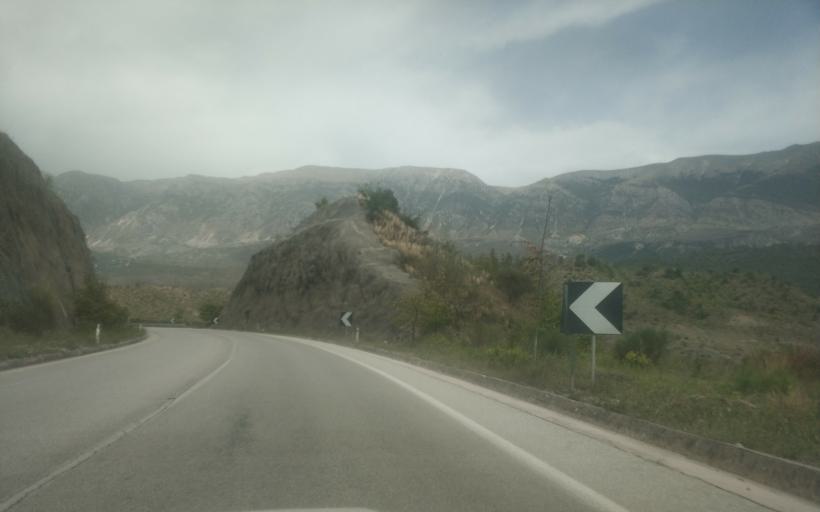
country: AL
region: Gjirokaster
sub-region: Rrethi i Gjirokastres
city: Picar
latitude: 40.2015
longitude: 20.0903
